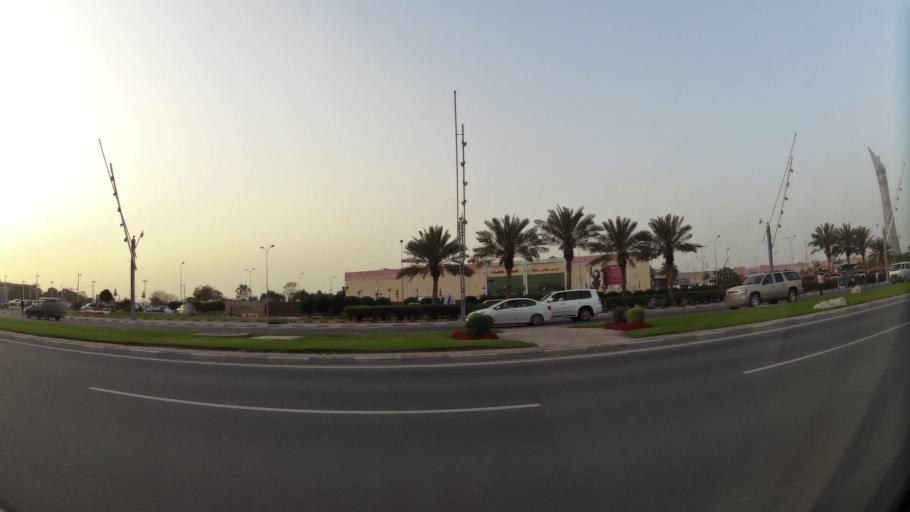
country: QA
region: Baladiyat ar Rayyan
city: Ar Rayyan
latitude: 25.2545
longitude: 51.4374
